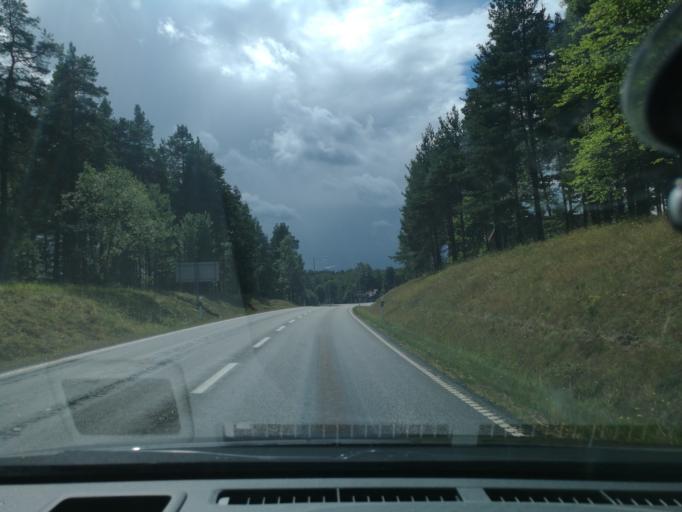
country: SE
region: OErebro
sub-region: Hallsbergs Kommun
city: Palsboda
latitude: 58.8997
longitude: 15.4351
